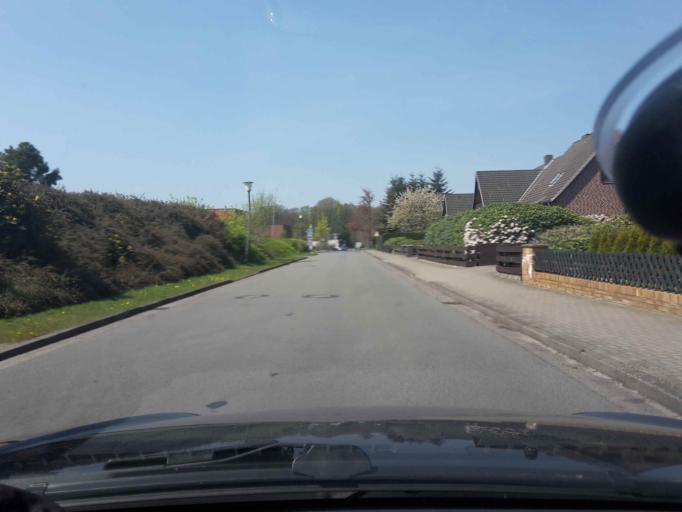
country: DE
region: Lower Saxony
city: Schneverdingen
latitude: 53.1080
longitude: 9.7928
